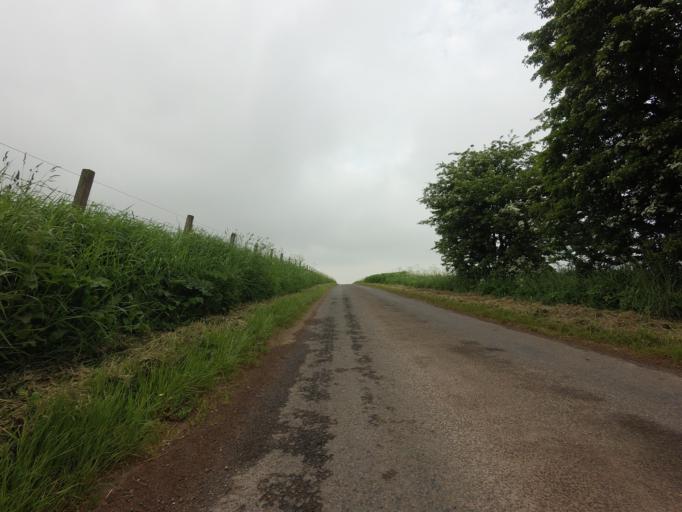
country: GB
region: Scotland
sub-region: Perth and Kinross
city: Milnathort
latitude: 56.2418
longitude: -3.3434
